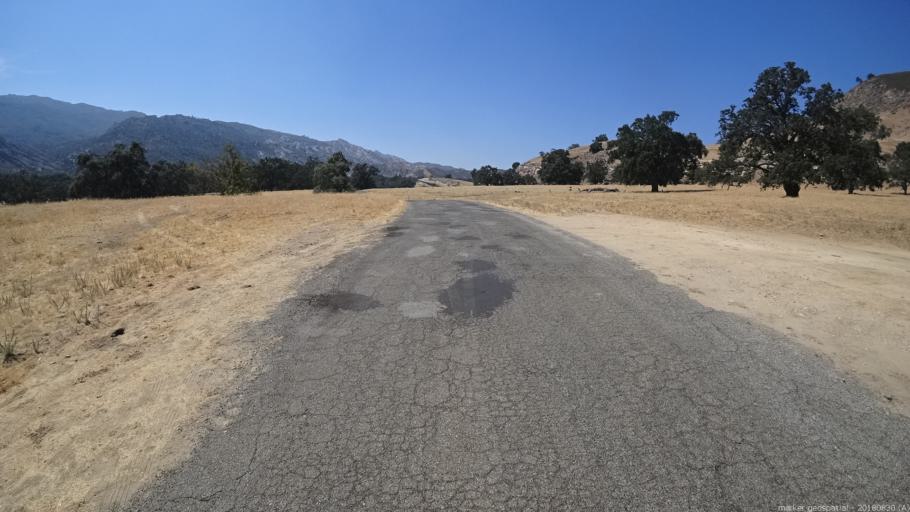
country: US
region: California
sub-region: Monterey County
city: Greenfield
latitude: 36.0996
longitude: -121.4281
